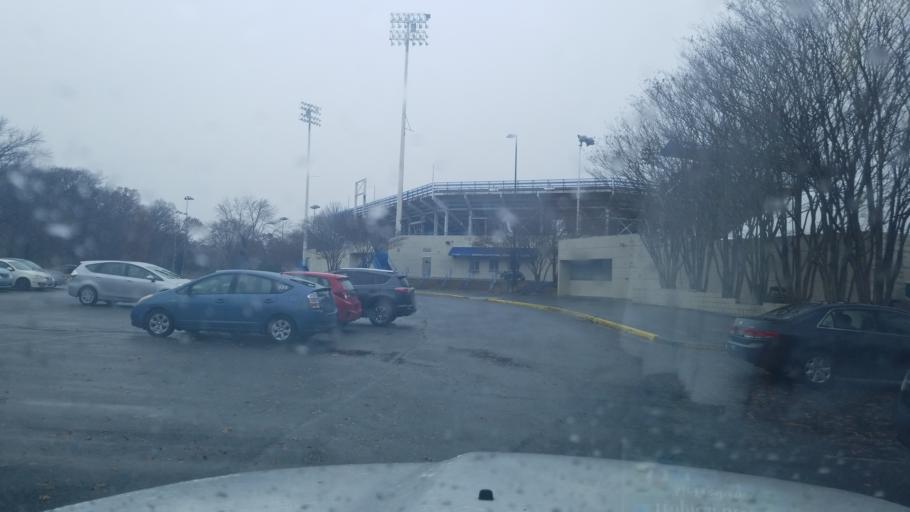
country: US
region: Maryland
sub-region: Montgomery County
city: Silver Spring
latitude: 38.9532
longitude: -77.0391
